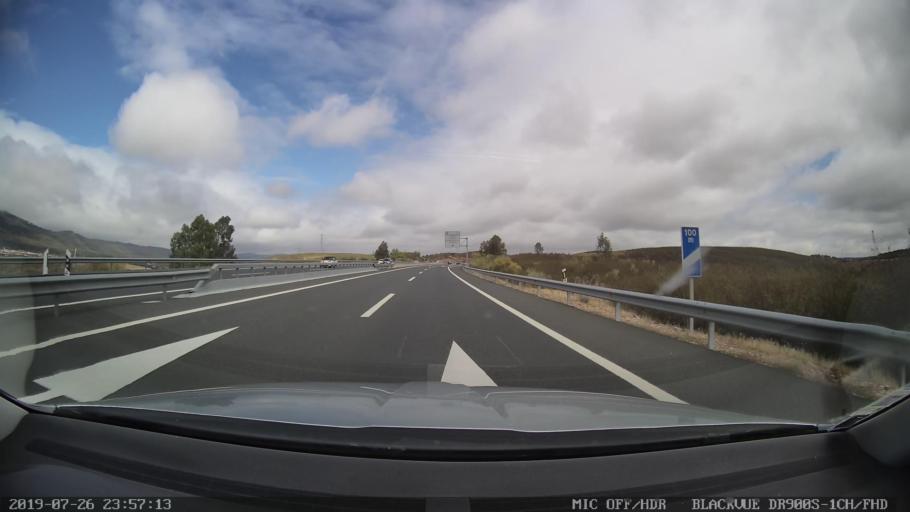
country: ES
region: Extremadura
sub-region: Provincia de Caceres
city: Romangordo
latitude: 39.7269
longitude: -5.7160
